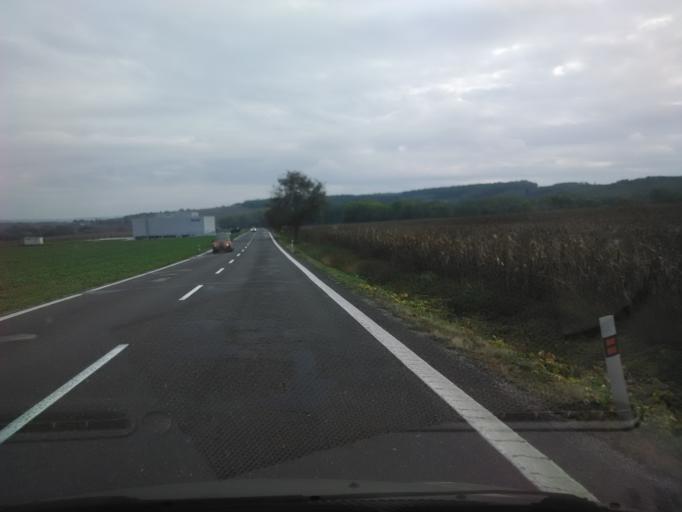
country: SK
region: Nitriansky
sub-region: Okres Nitra
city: Vrable
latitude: 48.2724
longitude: 18.2491
